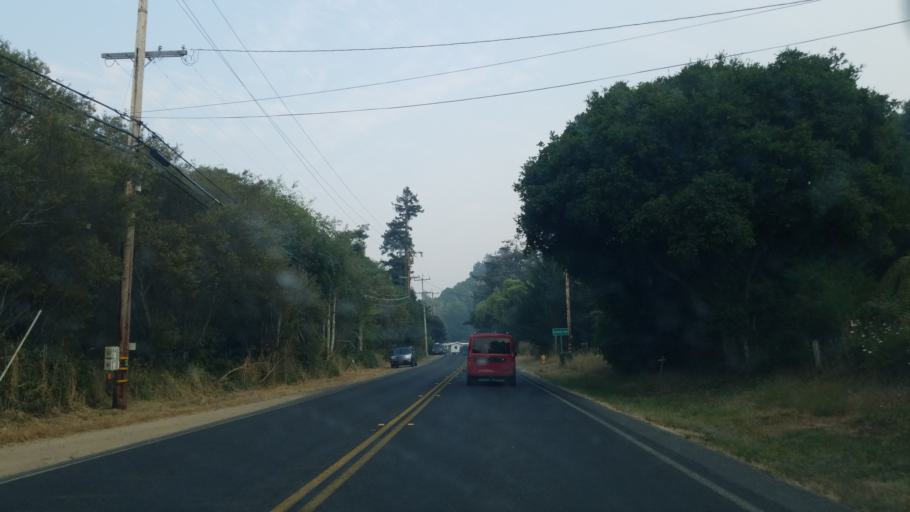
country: US
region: California
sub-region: Marin County
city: Inverness
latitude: 38.0713
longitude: -122.8260
